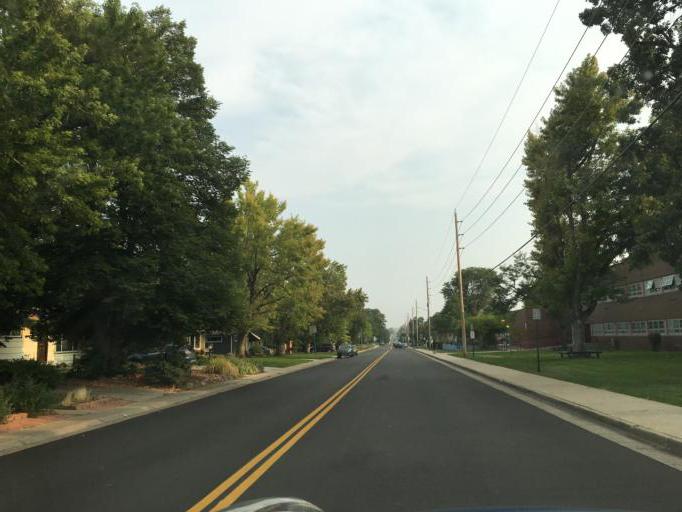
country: US
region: Colorado
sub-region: Arapahoe County
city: Glendale
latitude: 39.6872
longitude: -104.9317
